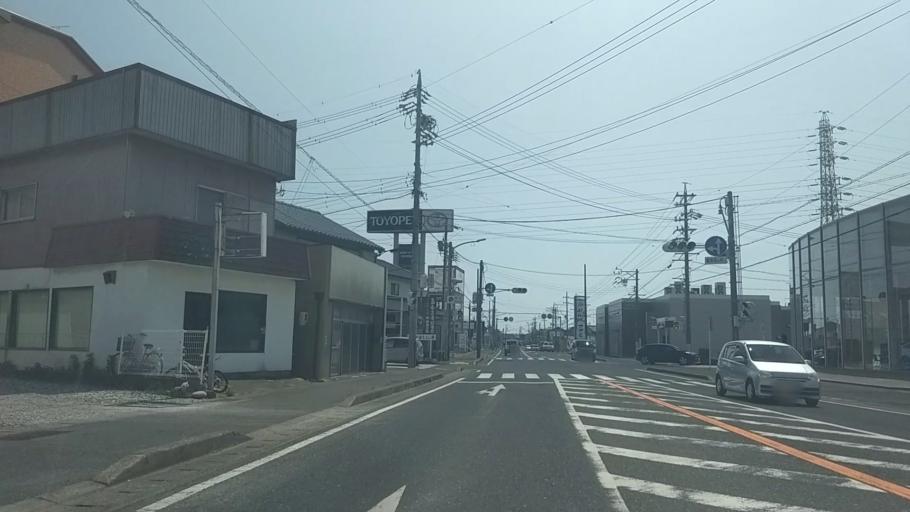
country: JP
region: Shizuoka
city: Hamamatsu
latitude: 34.6913
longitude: 137.7161
